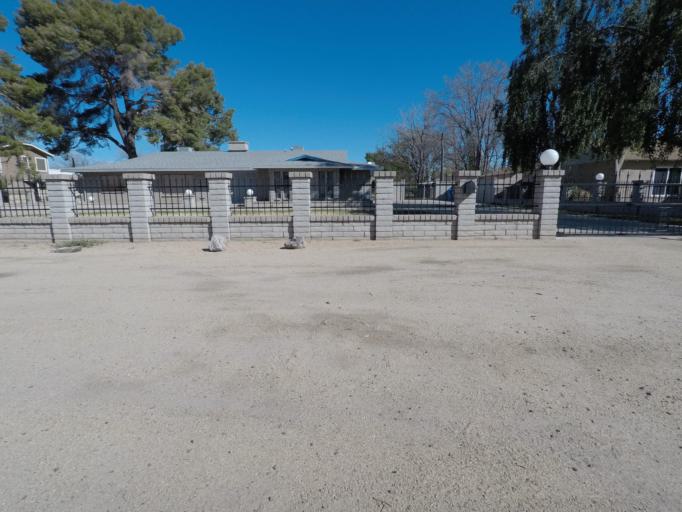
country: US
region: Arizona
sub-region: Maricopa County
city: Glendale
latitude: 33.5459
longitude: -112.1290
